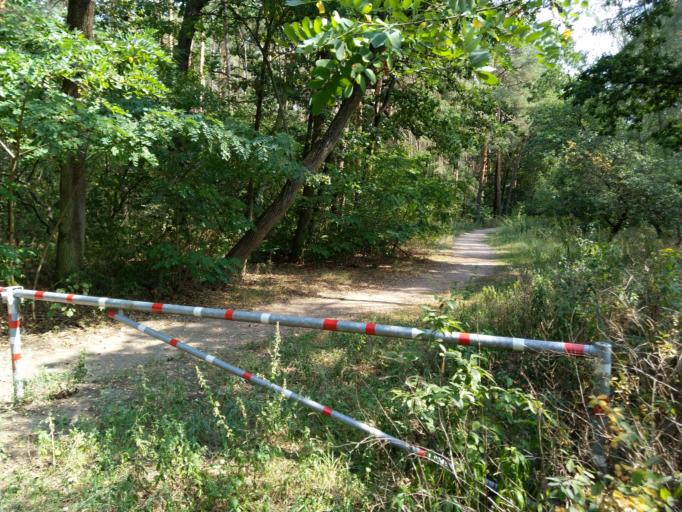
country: DE
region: Berlin
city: Friedrichshagen
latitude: 52.4704
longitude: 13.6127
